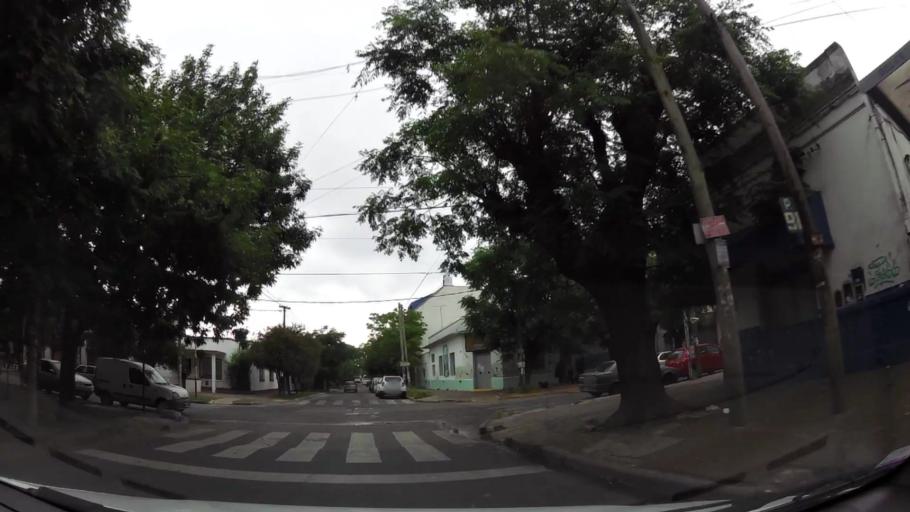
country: AR
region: Buenos Aires F.D.
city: Villa Lugano
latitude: -34.7079
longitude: -58.5153
